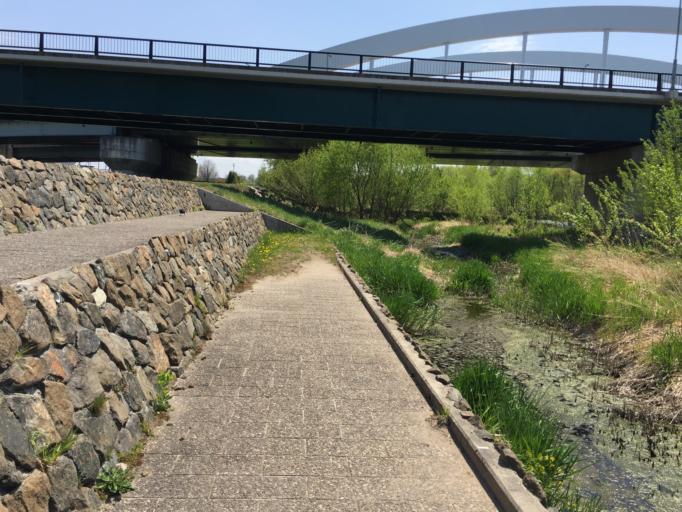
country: JP
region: Hokkaido
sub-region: Asahikawa-shi
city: Asahikawa
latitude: 43.7556
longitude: 142.3663
